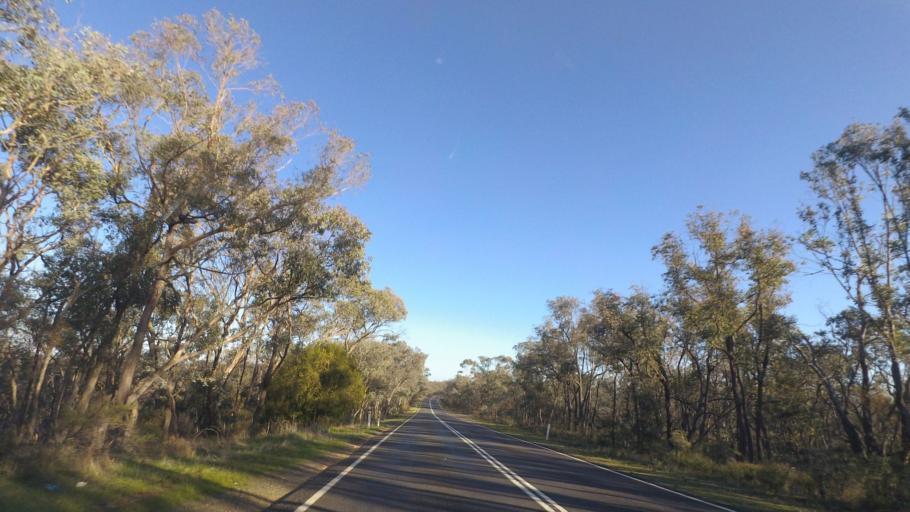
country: AU
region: Victoria
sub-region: Greater Bendigo
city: Kennington
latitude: -36.9271
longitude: 144.4892
